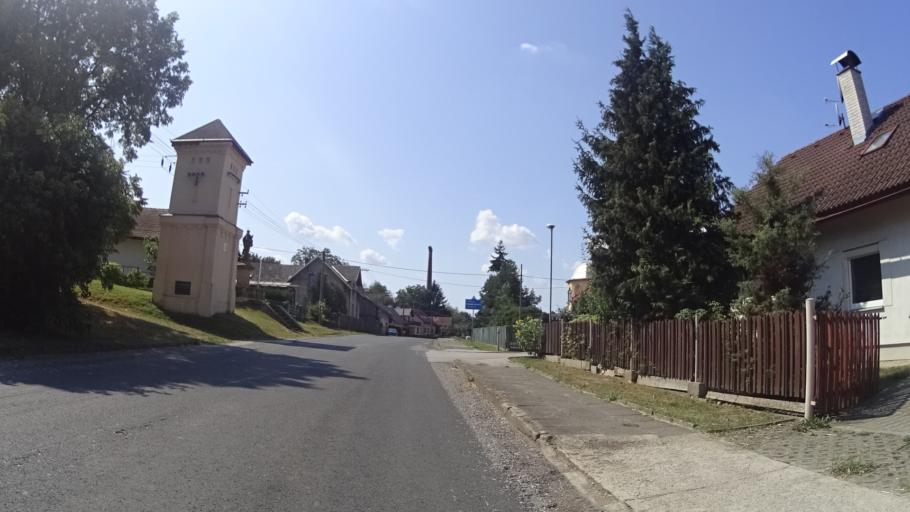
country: CZ
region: Kralovehradecky
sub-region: Okres Jicin
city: Jicin
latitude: 50.3680
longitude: 15.3853
